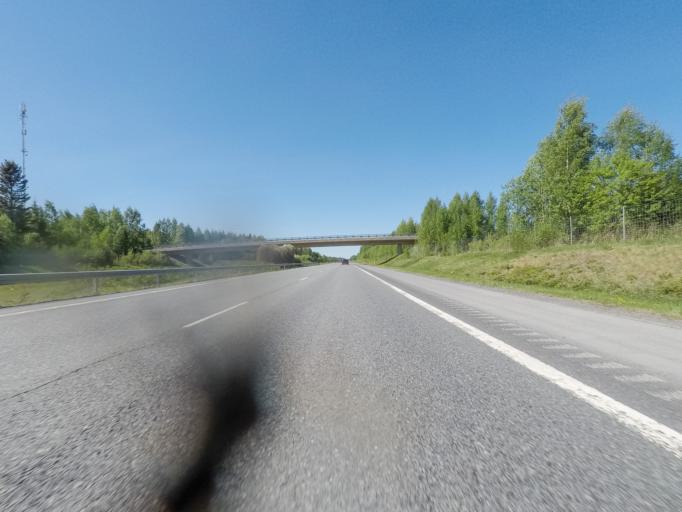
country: FI
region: Pirkanmaa
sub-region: Etelae-Pirkanmaa
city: Valkeakoski
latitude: 61.1478
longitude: 23.9994
